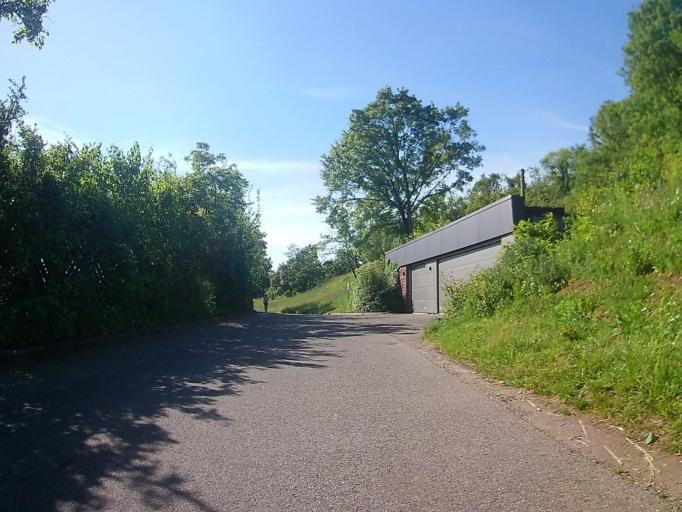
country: DE
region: Baden-Wuerttemberg
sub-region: Regierungsbezirk Stuttgart
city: Fellbach
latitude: 48.7839
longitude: 9.2867
